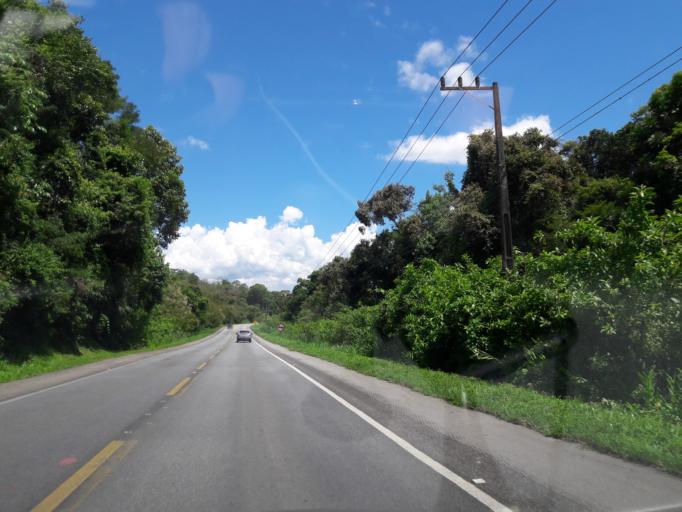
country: BR
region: Parana
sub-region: Antonina
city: Antonina
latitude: -25.4458
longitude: -48.7980
